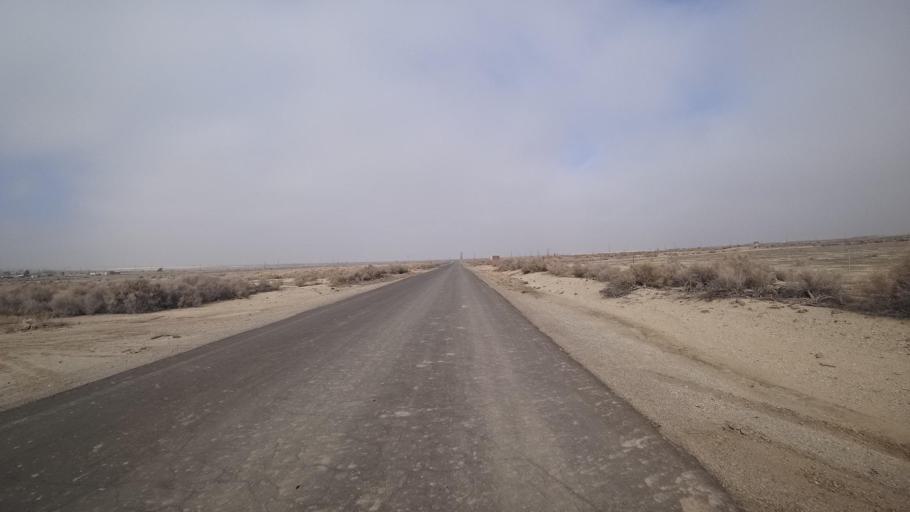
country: US
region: California
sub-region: Kern County
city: Maricopa
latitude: 35.0535
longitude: -119.3671
